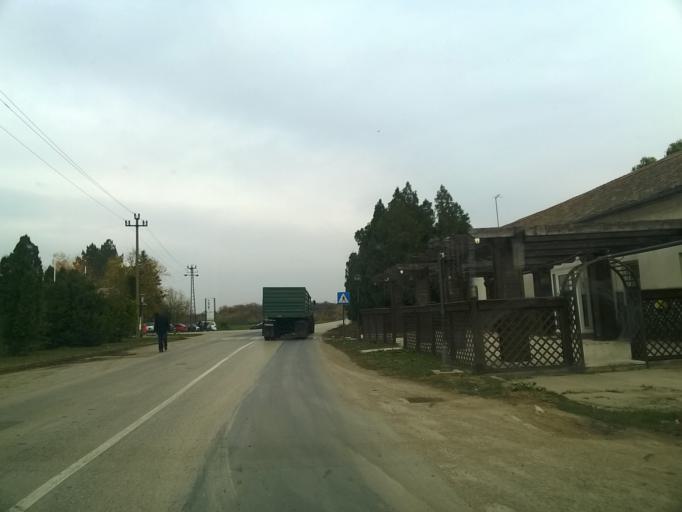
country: RS
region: Autonomna Pokrajina Vojvodina
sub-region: Juznobanatski Okrug
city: Pancevo
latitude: 44.9346
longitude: 20.6677
